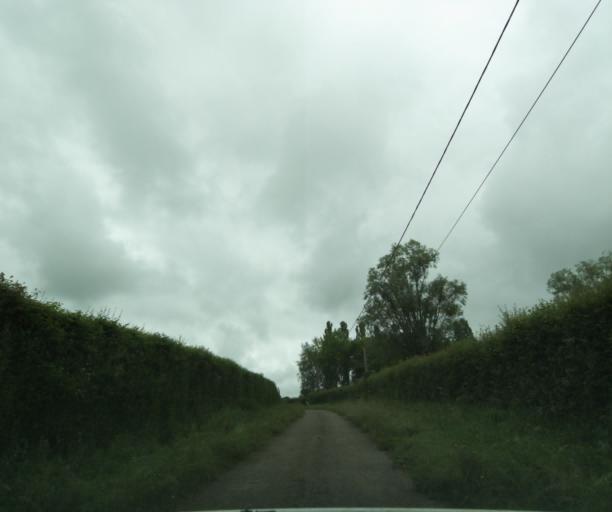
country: FR
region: Bourgogne
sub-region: Departement de Saone-et-Loire
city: Charolles
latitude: 46.4850
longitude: 4.3222
